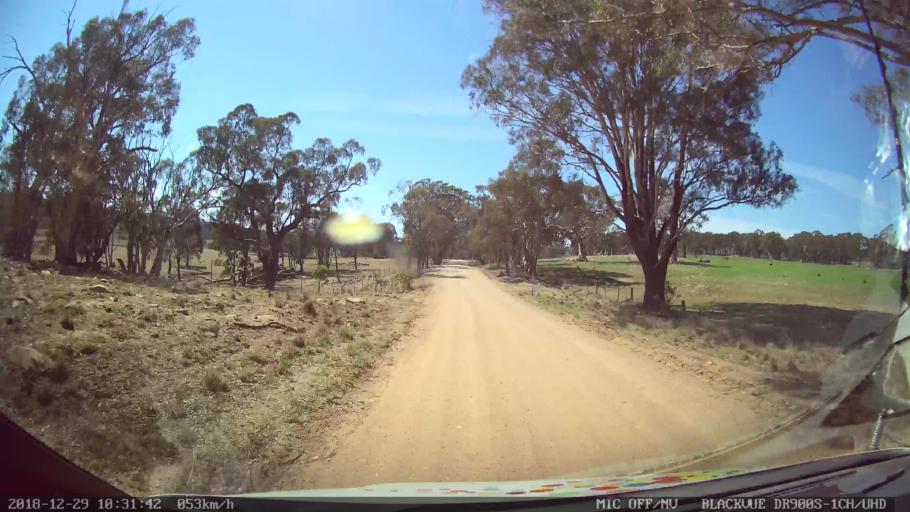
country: AU
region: New South Wales
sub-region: Yass Valley
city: Gundaroo
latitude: -34.9704
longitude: 149.4587
